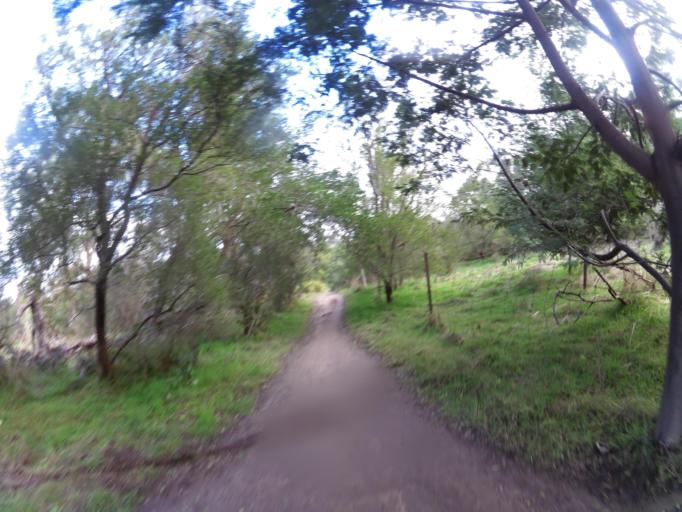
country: AU
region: Victoria
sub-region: Banyule
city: Lower Plenty
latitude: -37.7406
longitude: 145.1253
